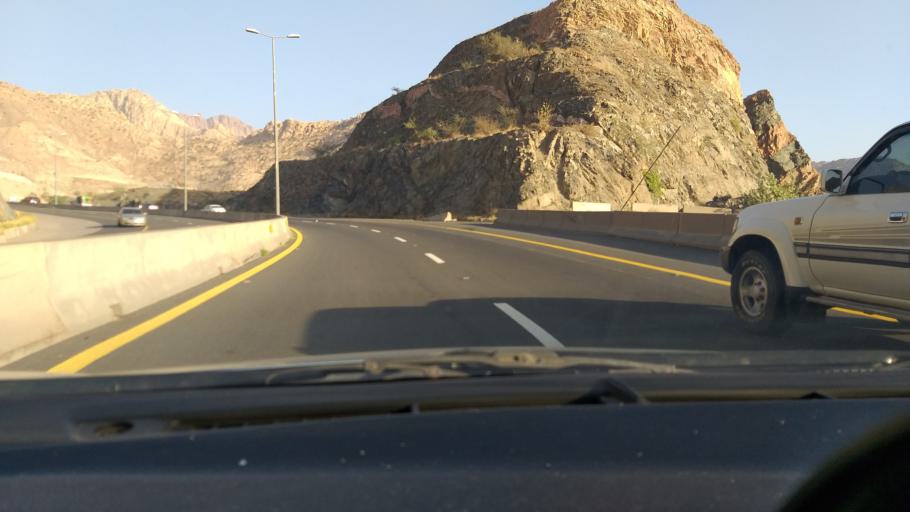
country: SA
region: Makkah
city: Al Hada
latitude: 21.3477
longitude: 40.2468
